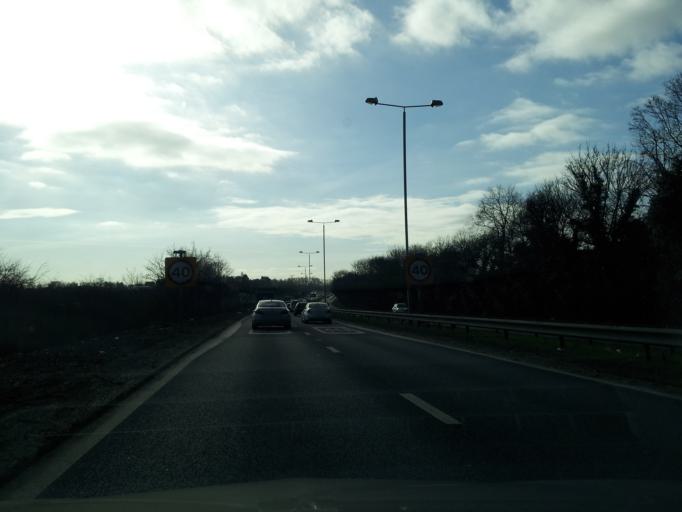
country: GB
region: England
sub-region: Derbyshire
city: Long Eaton
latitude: 52.9246
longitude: -1.2606
